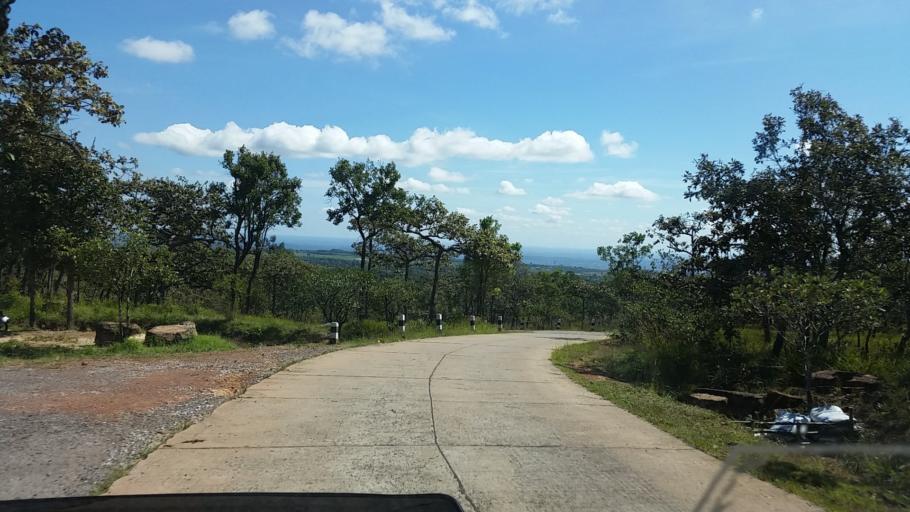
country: TH
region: Chaiyaphum
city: Sap Yai
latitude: 15.6419
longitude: 101.3881
